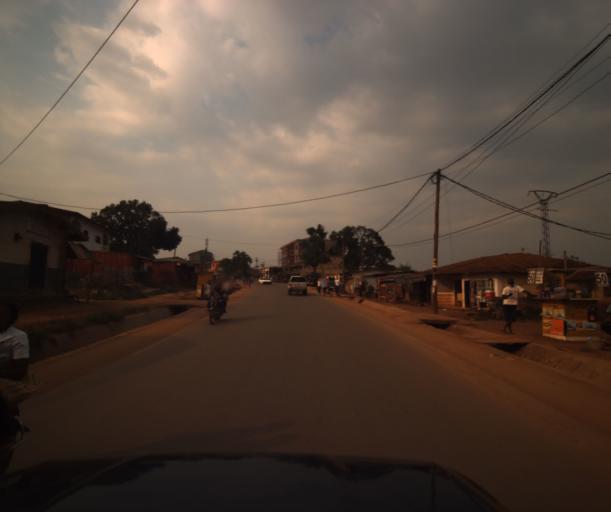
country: CM
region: Centre
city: Yaounde
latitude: 3.8289
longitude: 11.4713
